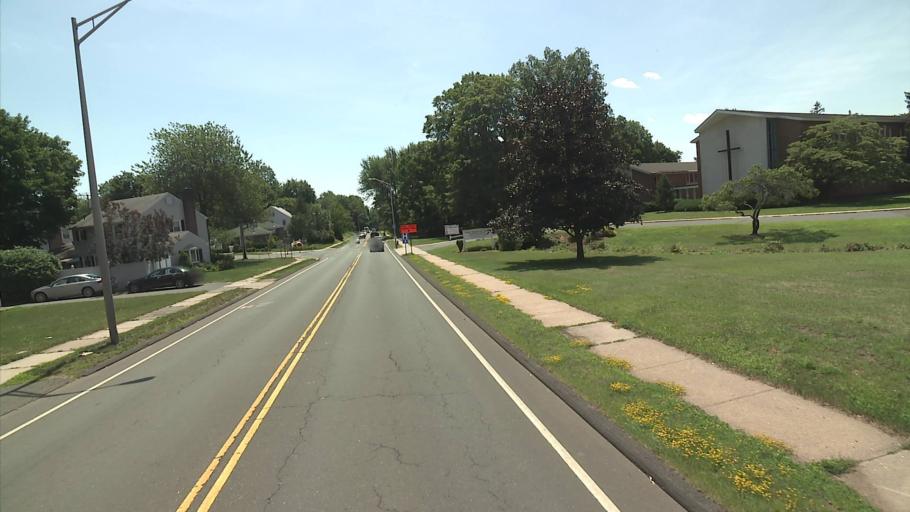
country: US
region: Connecticut
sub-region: Hartford County
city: New Britain
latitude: 41.6593
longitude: -72.8013
